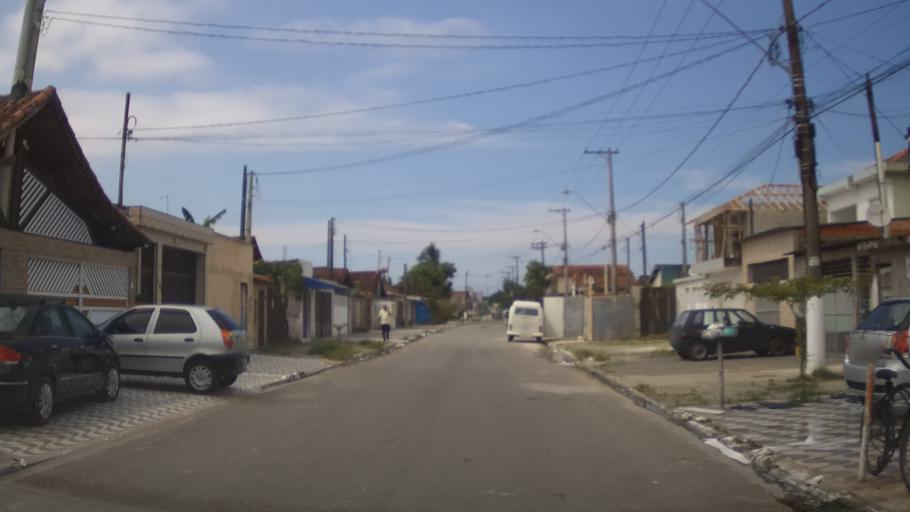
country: BR
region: Sao Paulo
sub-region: Praia Grande
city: Praia Grande
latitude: -24.0224
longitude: -46.4954
